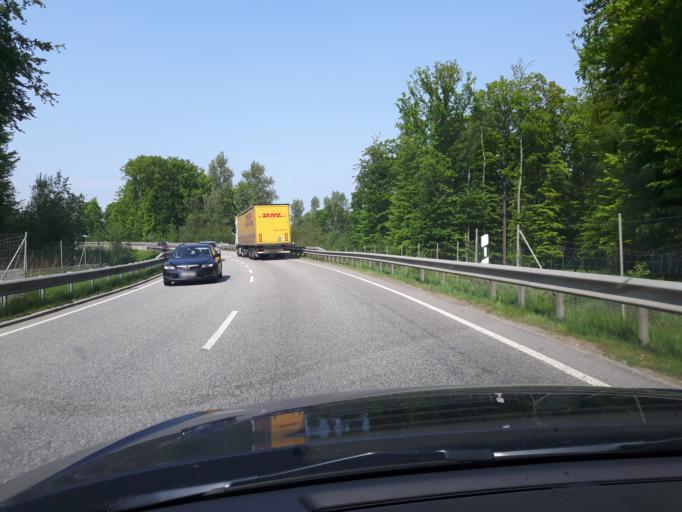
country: DE
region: Schleswig-Holstein
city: Ratekau
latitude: 53.8877
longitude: 10.7697
